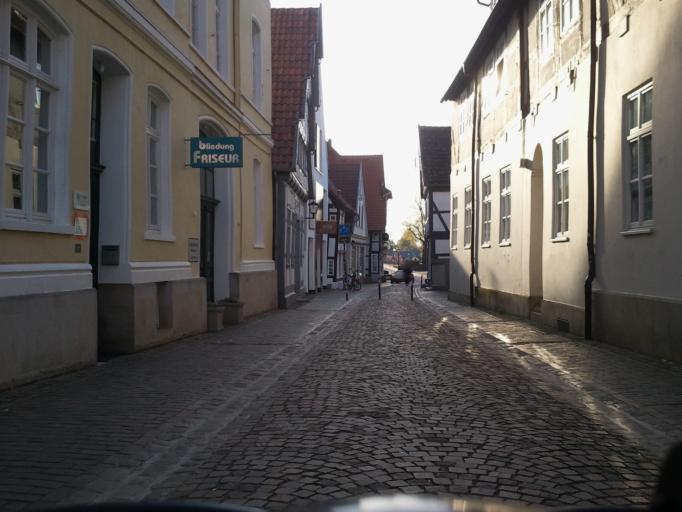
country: DE
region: Lower Saxony
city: Nienburg
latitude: 52.6391
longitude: 9.2051
